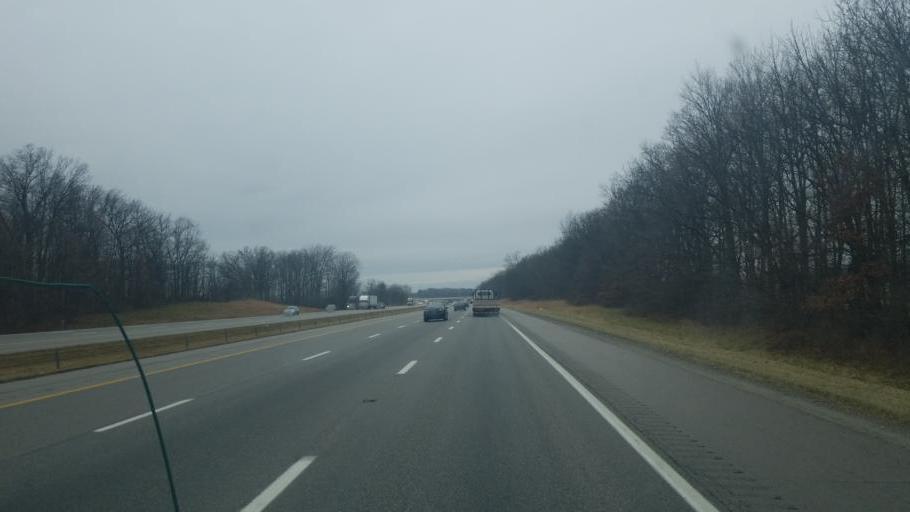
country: US
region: Ohio
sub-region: Madison County
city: Choctaw Lake
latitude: 39.9393
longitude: -83.5582
